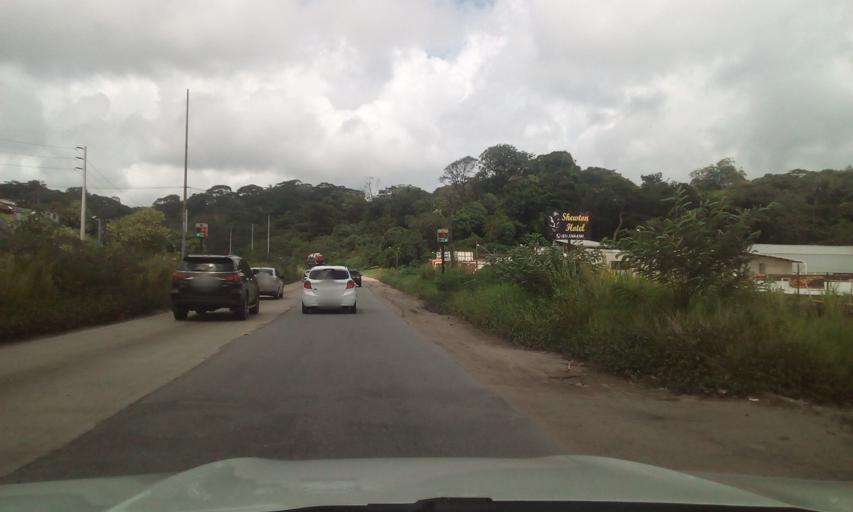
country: BR
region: Pernambuco
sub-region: Sao Lourenco Da Mata
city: Sao Lourenco da Mata
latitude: -7.9941
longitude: -34.9381
